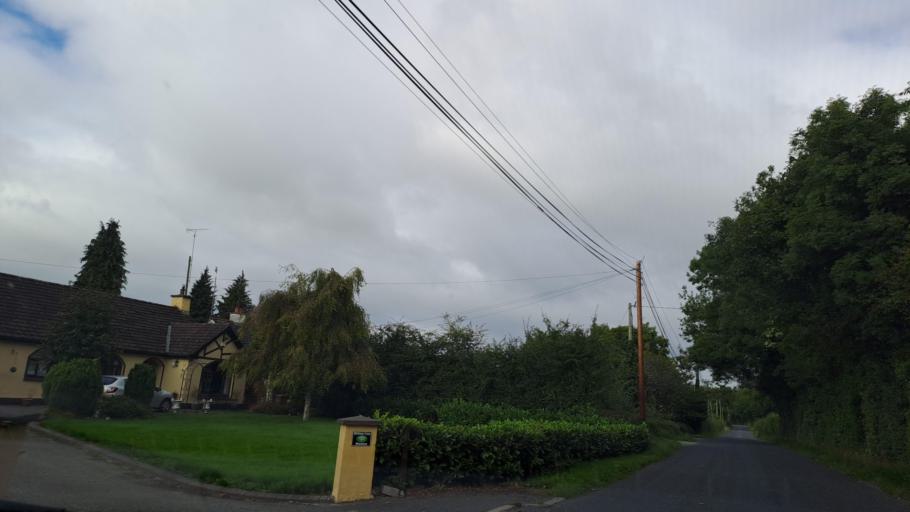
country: IE
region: Ulster
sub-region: County Monaghan
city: Carrickmacross
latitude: 53.9670
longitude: -6.7441
